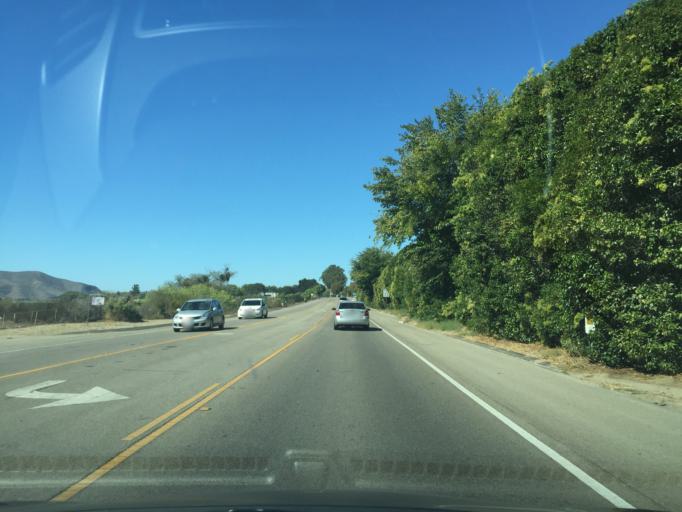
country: US
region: California
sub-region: Santa Barbara County
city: Buellton
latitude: 34.6066
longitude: -120.1762
